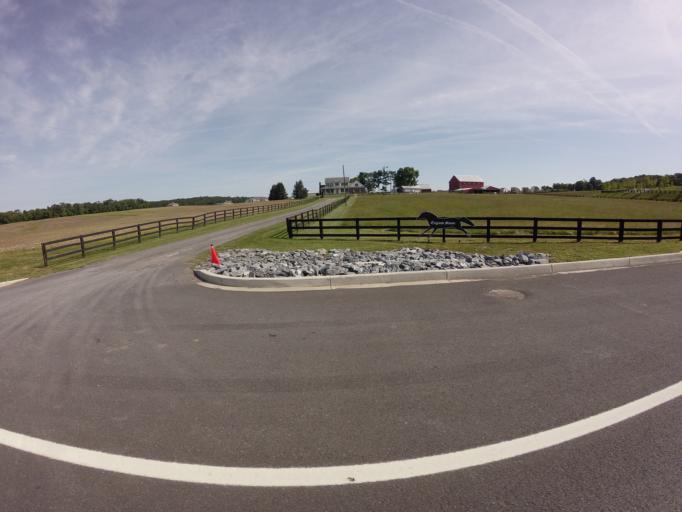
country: US
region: Maryland
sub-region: Frederick County
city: Green Valley
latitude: 39.3479
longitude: -77.2879
